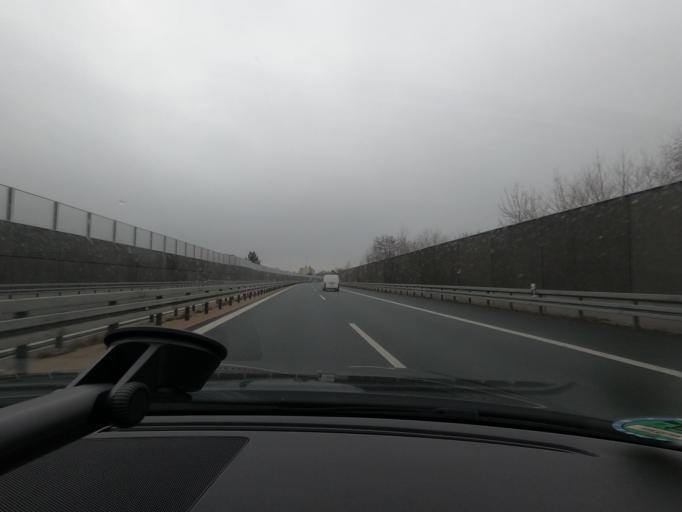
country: DE
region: Bavaria
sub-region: Upper Franconia
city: Forchheim
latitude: 49.7315
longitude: 11.0541
